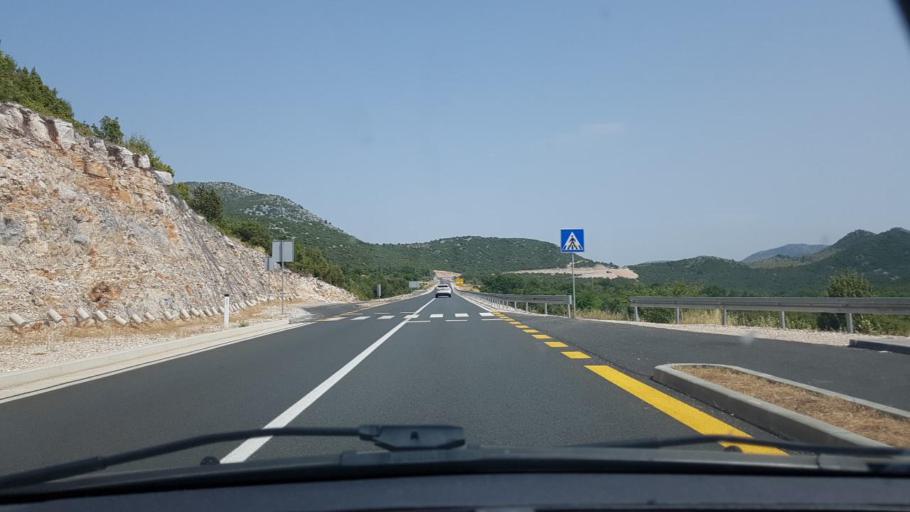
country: HR
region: Dubrovacko-Neretvanska
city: Ston
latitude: 42.9532
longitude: 17.7426
